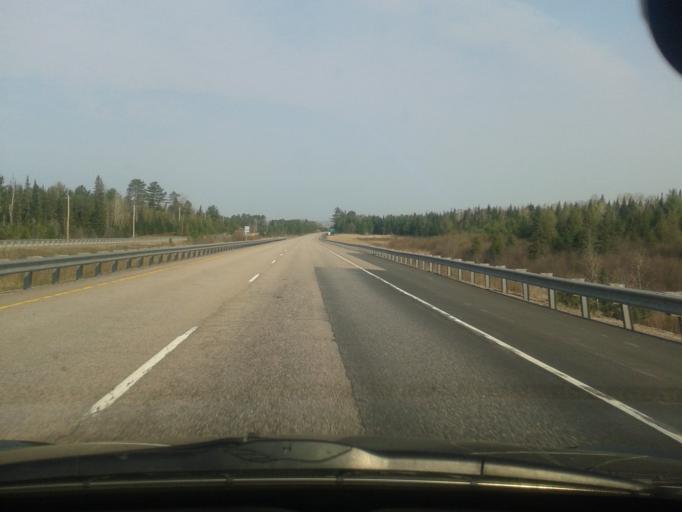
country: CA
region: Ontario
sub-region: Nipissing District
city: North Bay
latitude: 46.2506
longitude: -79.3710
